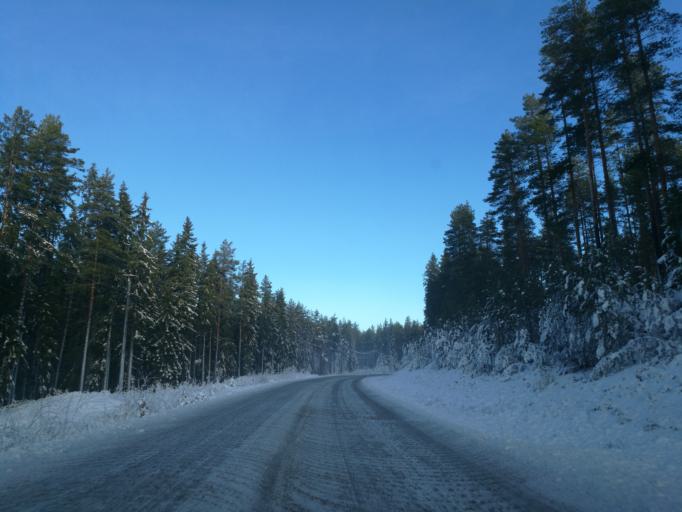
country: NO
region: Hedmark
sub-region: Grue
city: Kirkenaer
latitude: 60.3833
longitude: 12.3589
